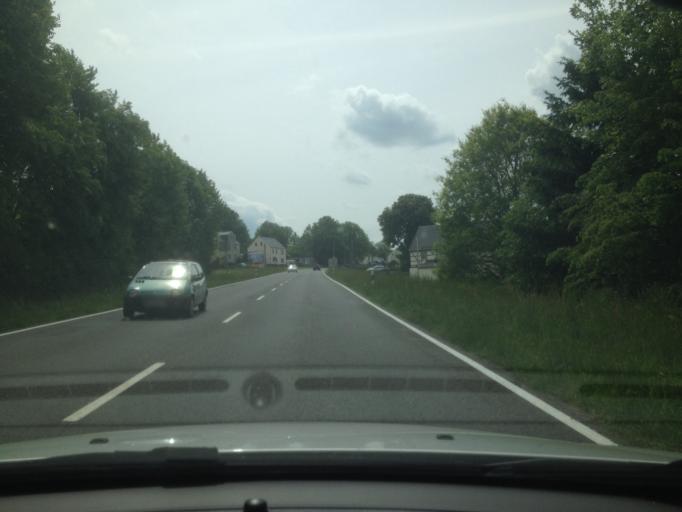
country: DE
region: Saxony
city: Stollberg
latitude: 50.6940
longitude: 12.7685
